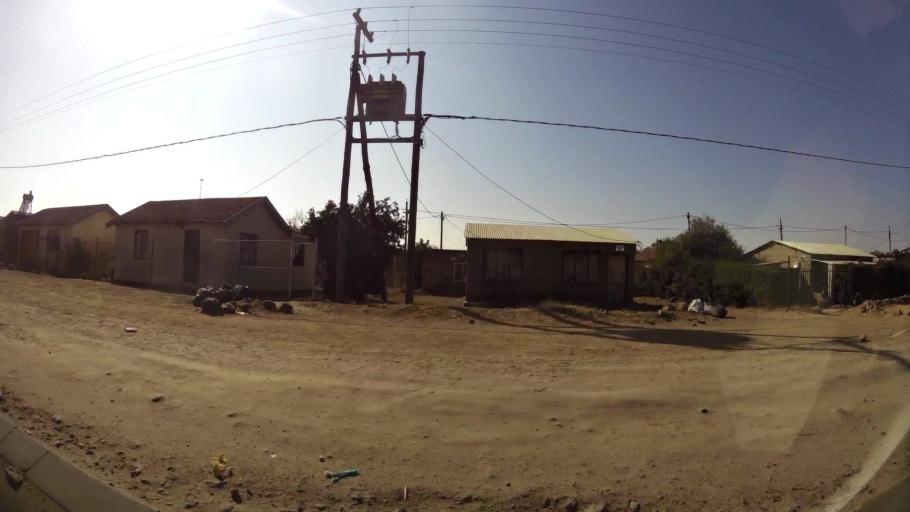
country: ZA
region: Orange Free State
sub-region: Mangaung Metropolitan Municipality
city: Bloemfontein
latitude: -29.1981
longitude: 26.2485
